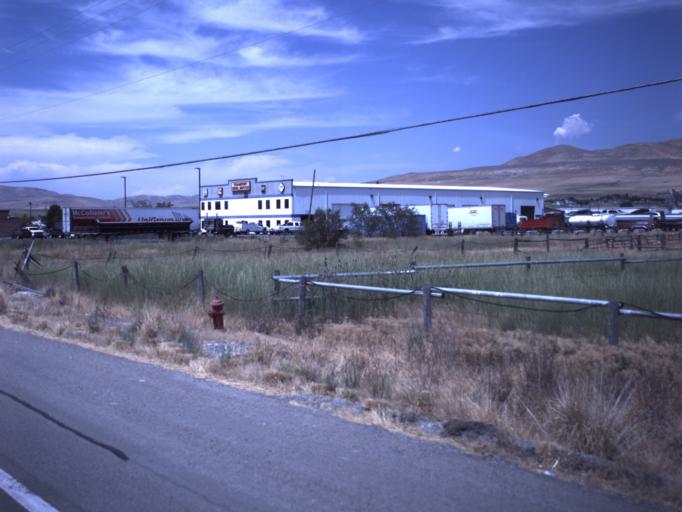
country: US
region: Utah
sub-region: Box Elder County
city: Tremonton
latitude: 41.7110
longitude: -112.1981
